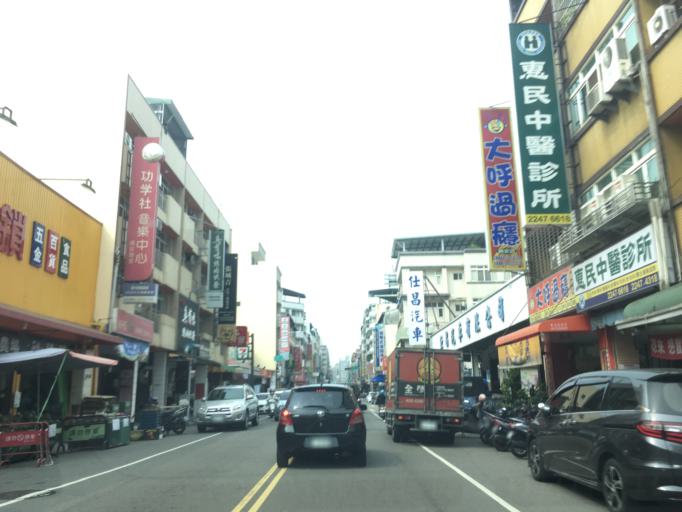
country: TW
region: Taiwan
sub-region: Taichung City
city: Taichung
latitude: 24.1725
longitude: 120.6944
